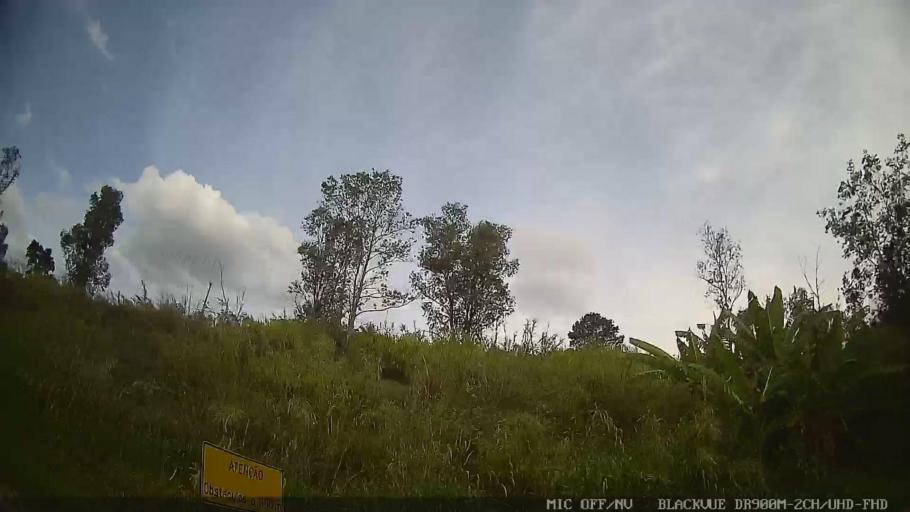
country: BR
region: Sao Paulo
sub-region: Amparo
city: Amparo
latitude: -22.7272
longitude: -46.7678
